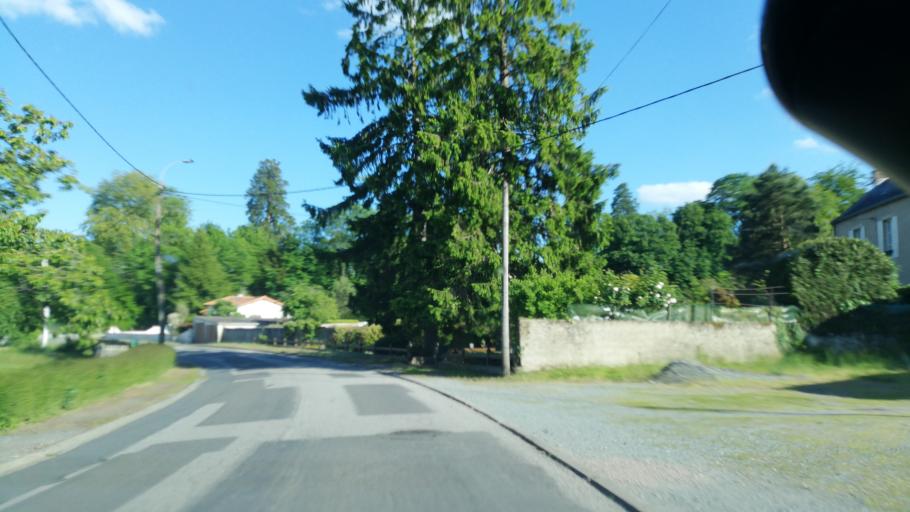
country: FR
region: Poitou-Charentes
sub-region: Departement des Deux-Sevres
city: La Chapelle-Saint-Laurent
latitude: 46.7459
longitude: -0.4813
